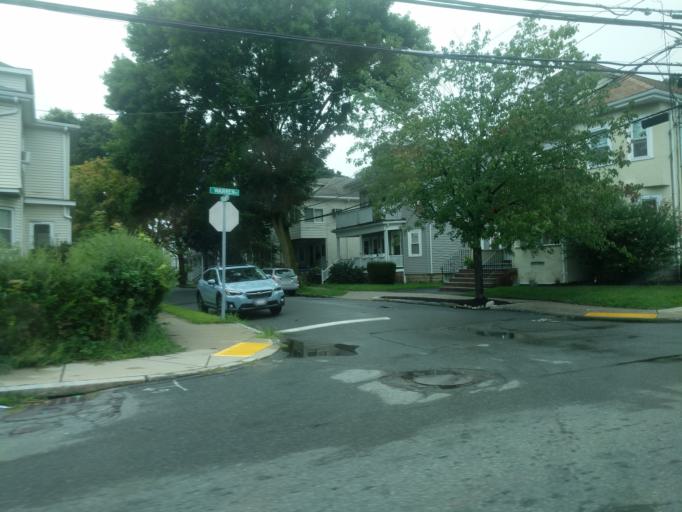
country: US
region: Massachusetts
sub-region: Middlesex County
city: Arlington
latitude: 42.4141
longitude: -71.1458
